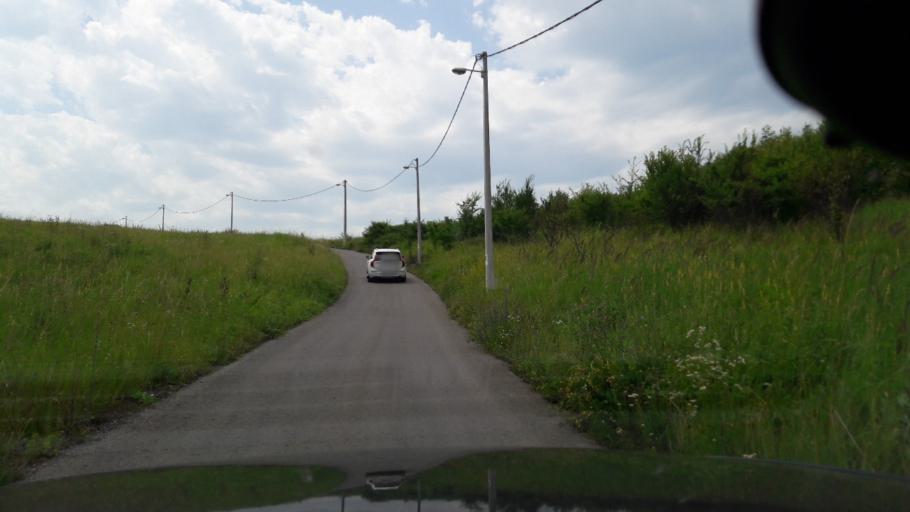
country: RS
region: Central Serbia
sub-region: Belgrade
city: Sopot
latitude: 44.6222
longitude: 20.6014
